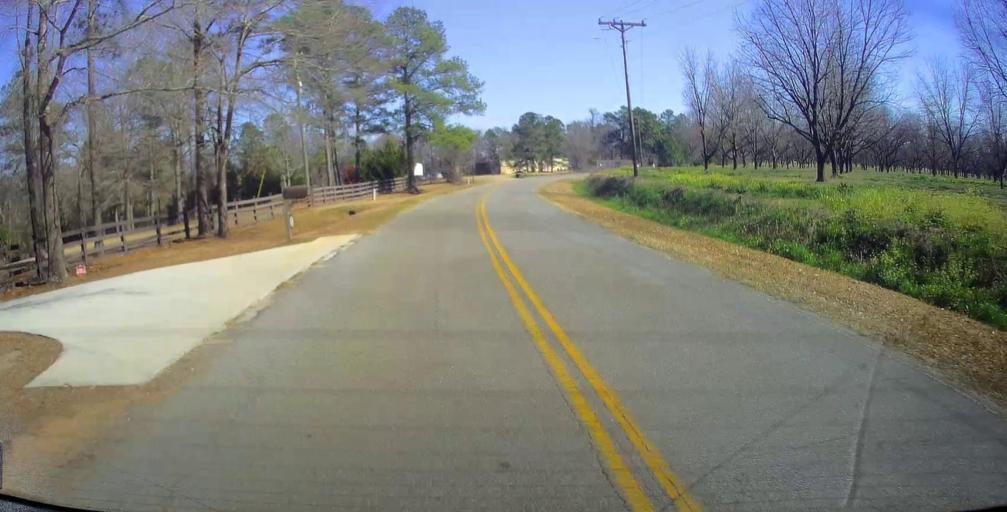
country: US
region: Georgia
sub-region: Peach County
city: Fort Valley
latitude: 32.6324
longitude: -83.8524
